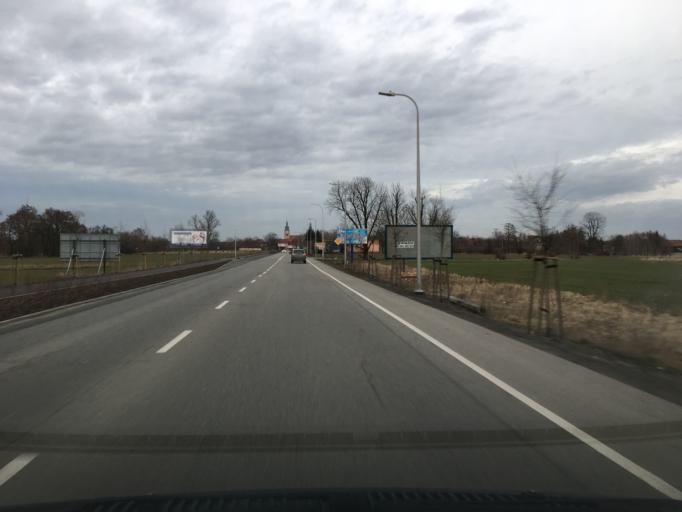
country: PL
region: Opole Voivodeship
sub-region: Powiat kedzierzynsko-kozielski
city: Kozle
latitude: 50.3406
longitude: 18.1625
